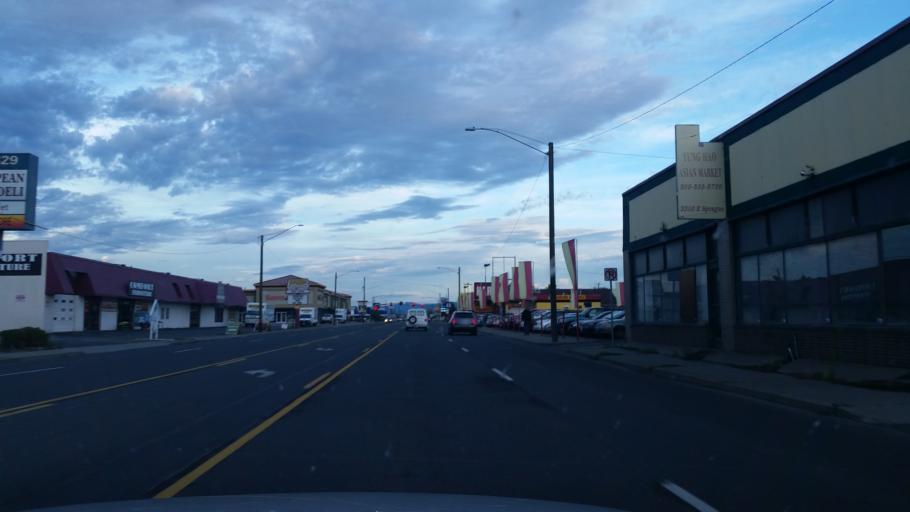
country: US
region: Washington
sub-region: Spokane County
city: Spokane
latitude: 47.6573
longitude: -117.3615
